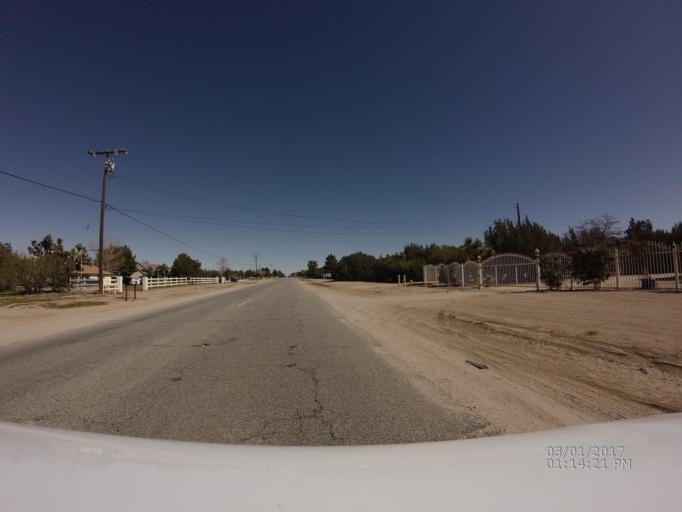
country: US
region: California
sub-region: Los Angeles County
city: Desert View Highlands
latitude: 34.6164
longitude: -118.1726
